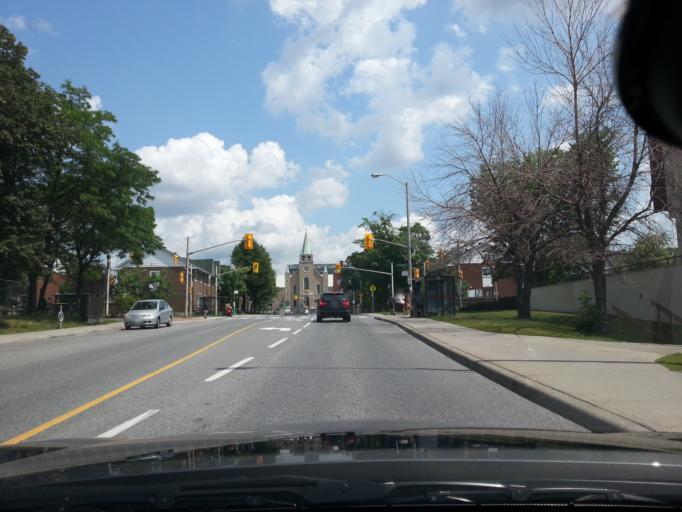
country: CA
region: Ontario
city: Ottawa
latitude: 45.4051
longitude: -75.7104
